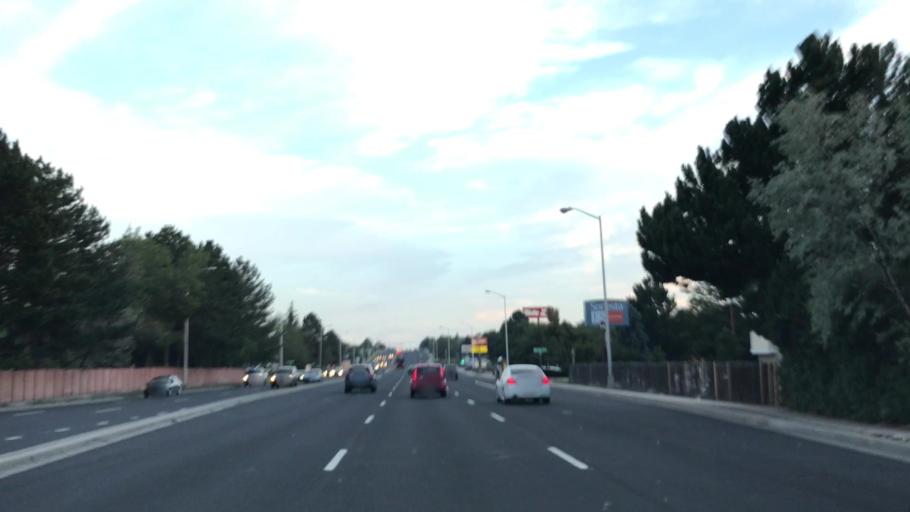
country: US
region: Colorado
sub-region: El Paso County
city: Cimarron Hills
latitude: 38.8875
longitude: -104.7571
